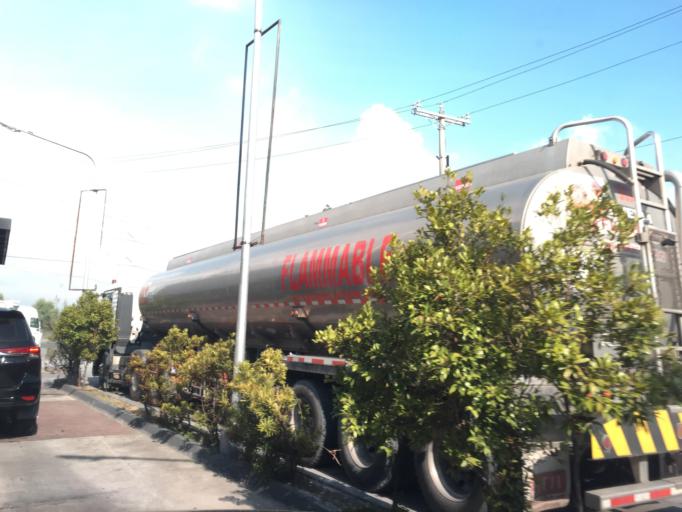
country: PH
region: Central Luzon
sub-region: Province of Bulacan
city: Guiguinto
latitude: 14.8312
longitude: 120.9080
